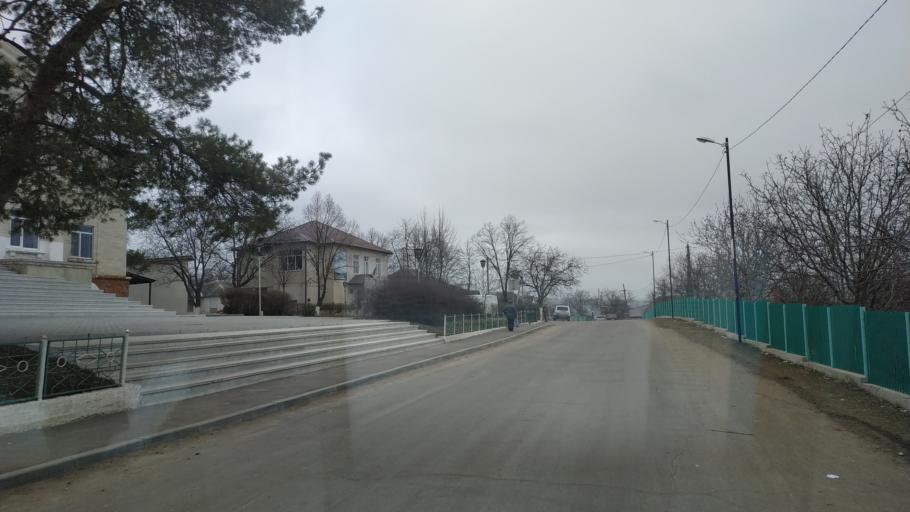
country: MD
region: Hincesti
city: Hincesti
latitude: 46.9802
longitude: 28.4698
